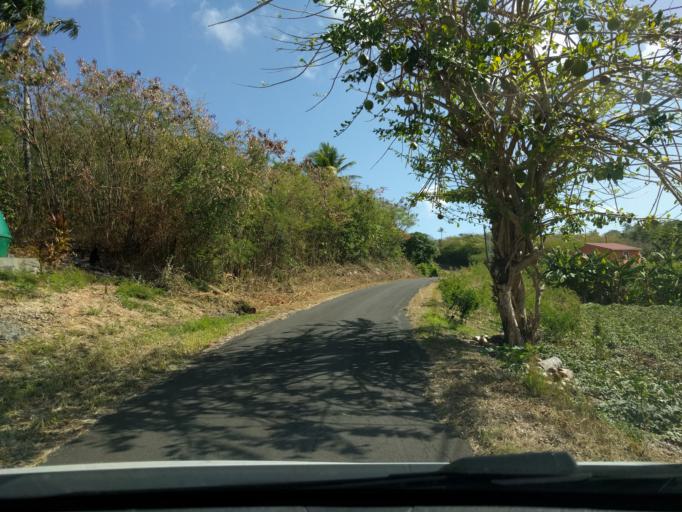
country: GP
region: Guadeloupe
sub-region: Guadeloupe
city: Grand-Bourg
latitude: 15.9762
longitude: -61.2559
